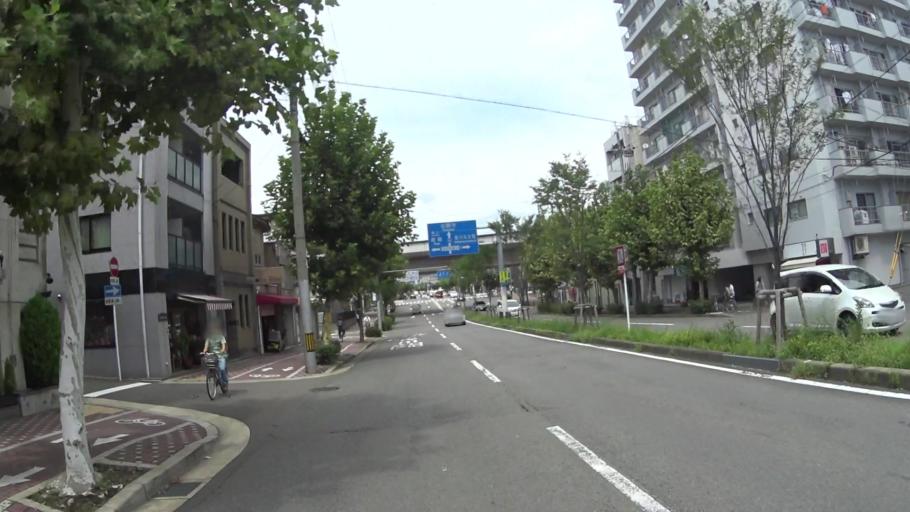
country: JP
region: Kyoto
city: Kyoto
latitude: 35.0171
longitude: 135.7317
